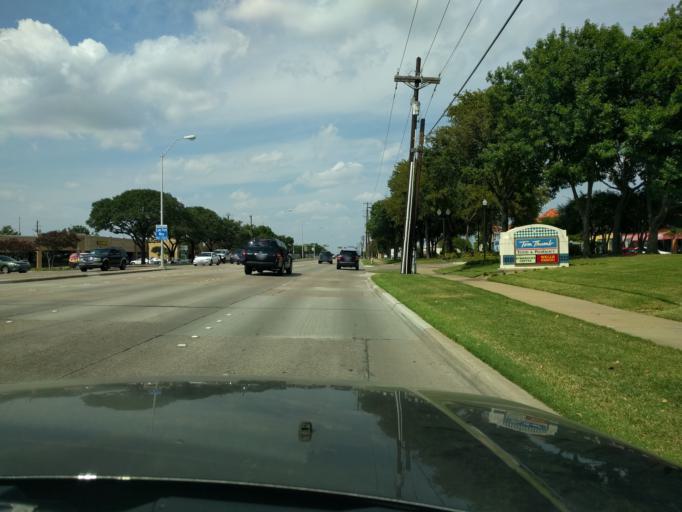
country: US
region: Texas
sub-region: Dallas County
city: Richardson
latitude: 32.9792
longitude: -96.7680
